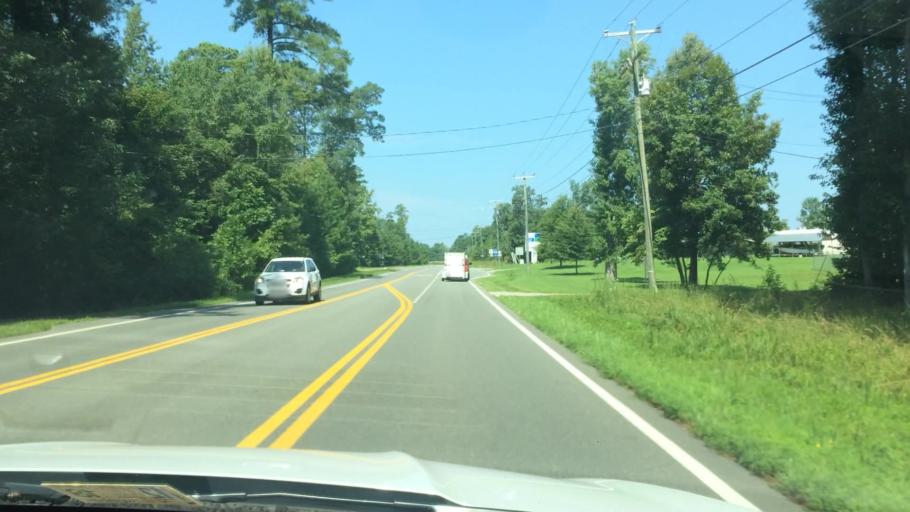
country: US
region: Virginia
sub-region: New Kent County
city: New Kent
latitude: 37.5229
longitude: -77.0068
